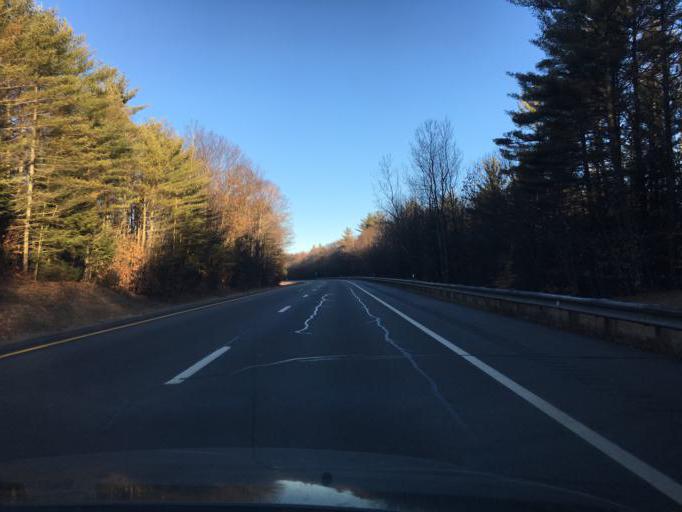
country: US
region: New Hampshire
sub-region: Belknap County
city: Sanbornton
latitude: 43.4890
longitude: -71.5948
